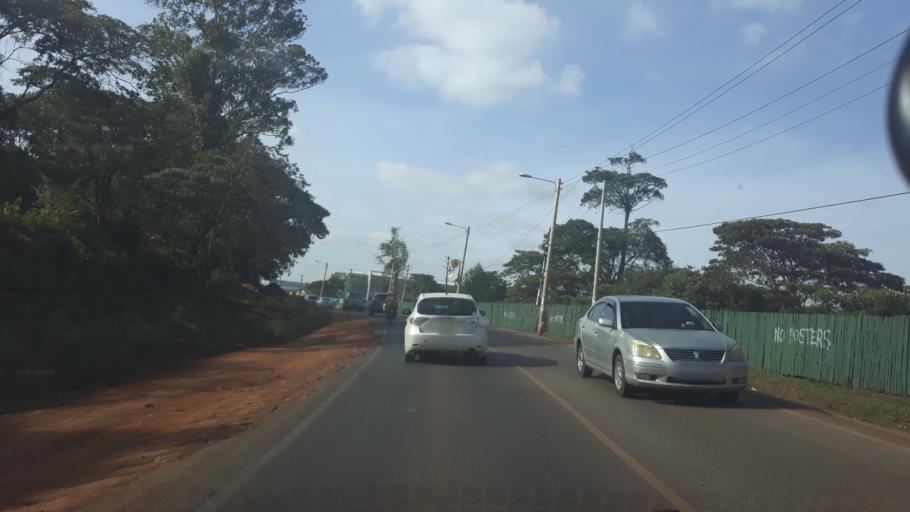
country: KE
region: Nairobi Area
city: Pumwani
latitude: -1.2325
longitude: 36.8432
